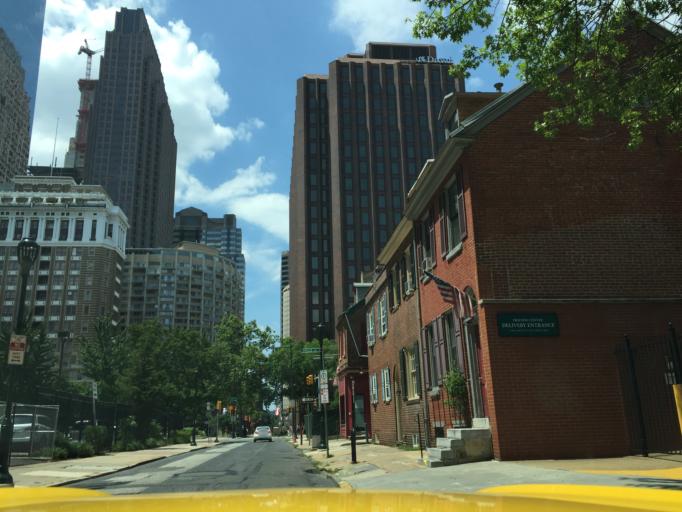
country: US
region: Pennsylvania
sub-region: Philadelphia County
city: Philadelphia
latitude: 39.9557
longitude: -75.1654
